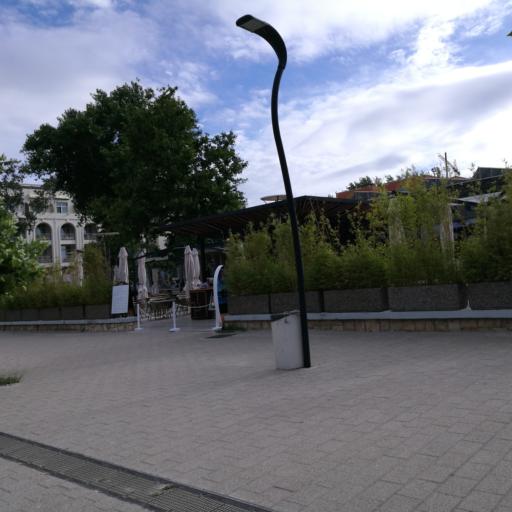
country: RO
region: Constanta
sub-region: Municipiul Constanta
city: Palazu Mare
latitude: 44.2449
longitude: 28.6226
